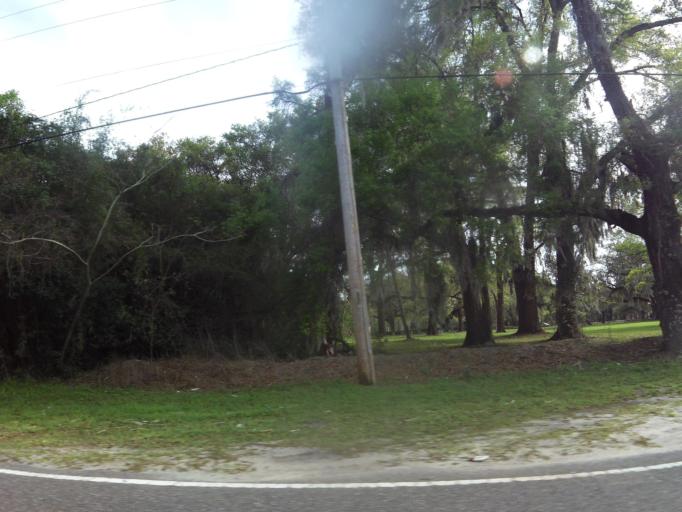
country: US
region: Florida
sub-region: Duval County
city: Jacksonville
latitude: 30.2985
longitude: -81.7658
